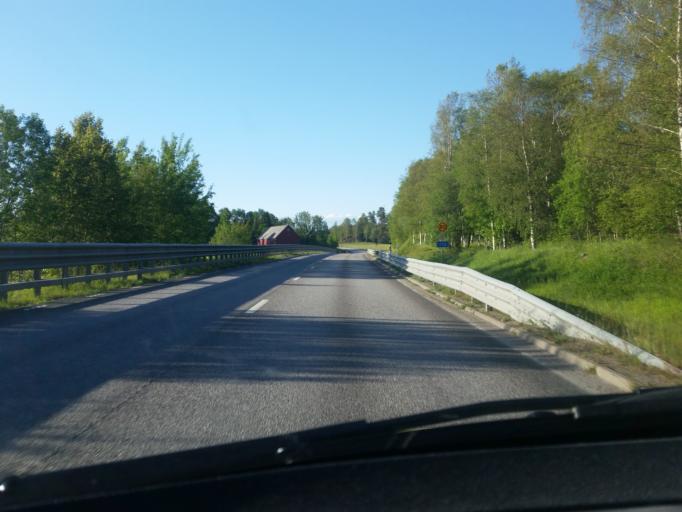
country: SE
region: Vaestra Goetaland
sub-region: Fargelanda Kommun
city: Faergelanda
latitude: 58.5473
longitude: 11.9905
